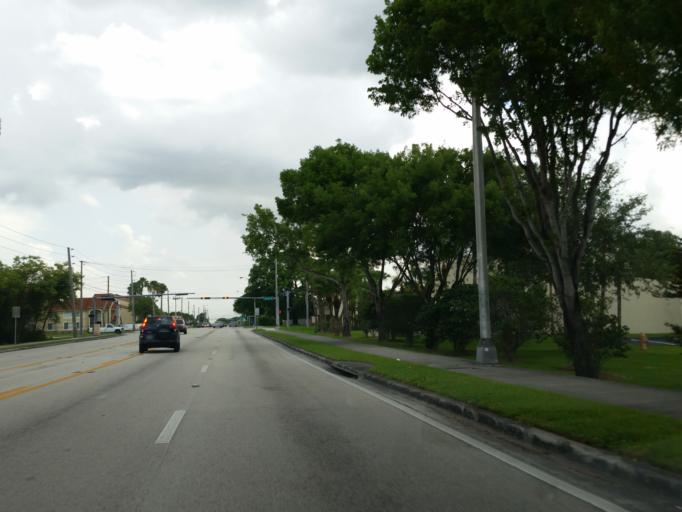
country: US
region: Florida
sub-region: Miami-Dade County
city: Sunset
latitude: 25.6960
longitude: -80.3660
